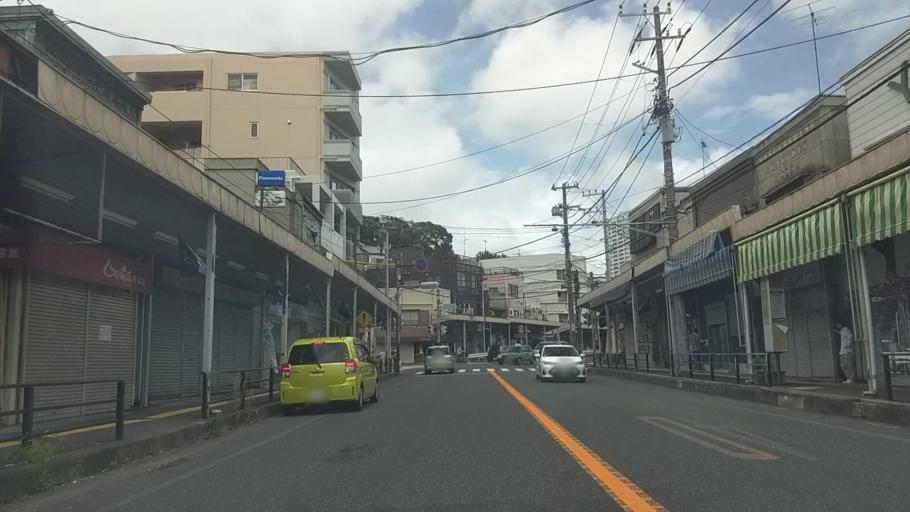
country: JP
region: Kanagawa
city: Yokosuka
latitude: 35.2752
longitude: 139.6699
